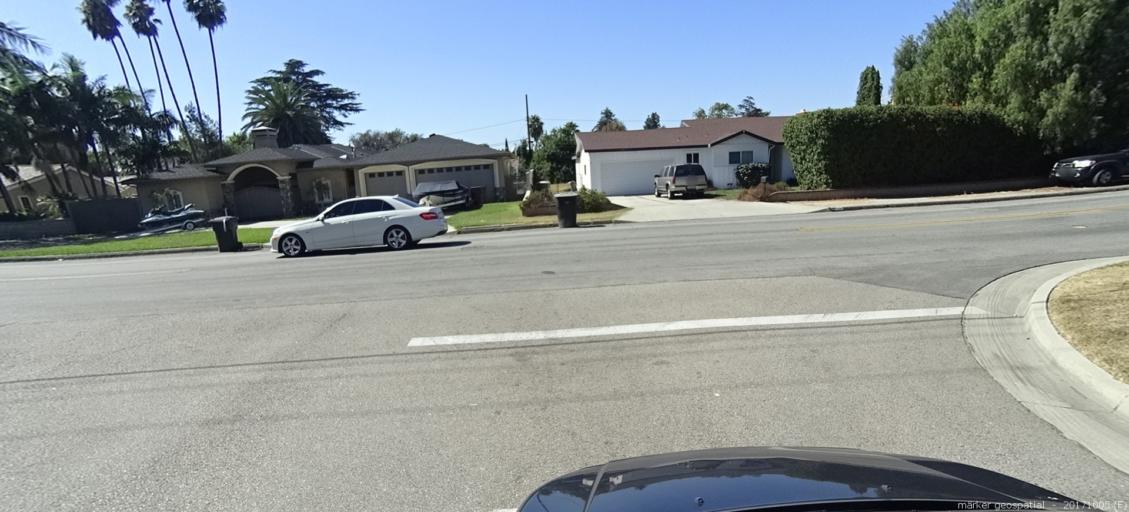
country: US
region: California
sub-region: Orange County
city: Garden Grove
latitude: 33.7835
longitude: -117.9672
